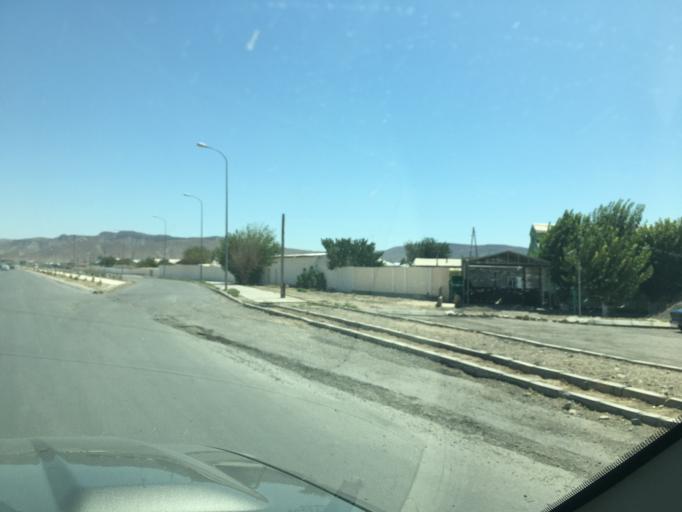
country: TM
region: Balkan
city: Serdar
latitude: 38.9904
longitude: 56.2870
